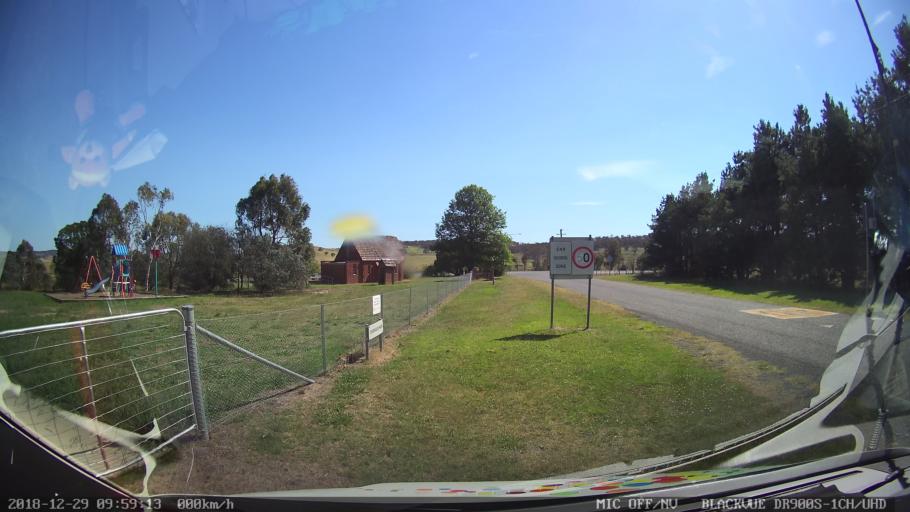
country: AU
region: New South Wales
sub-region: Goulburn Mulwaree
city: Goulburn
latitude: -34.7895
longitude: 149.4877
